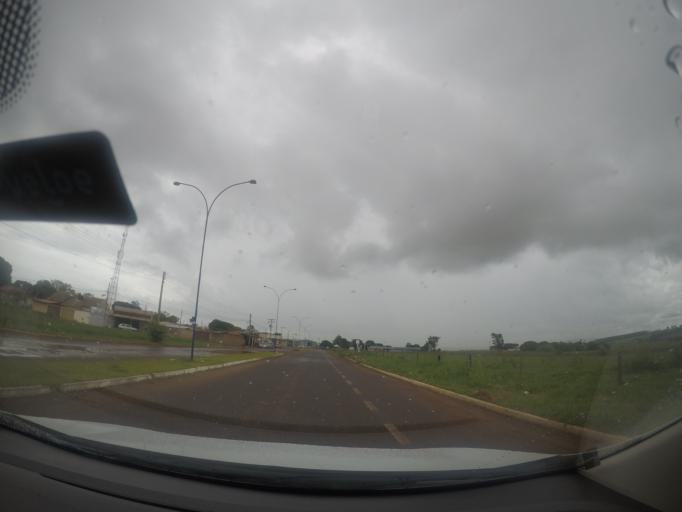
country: BR
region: Goias
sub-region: Trindade
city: Trindade
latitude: -16.6388
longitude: -49.4106
